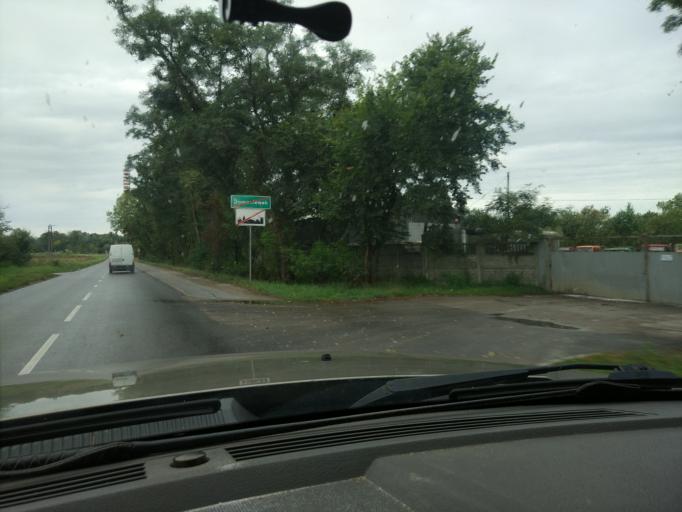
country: PL
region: Masovian Voivodeship
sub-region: Powiat warszawski zachodni
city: Ozarow Mazowiecki
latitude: 52.1888
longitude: 20.7530
